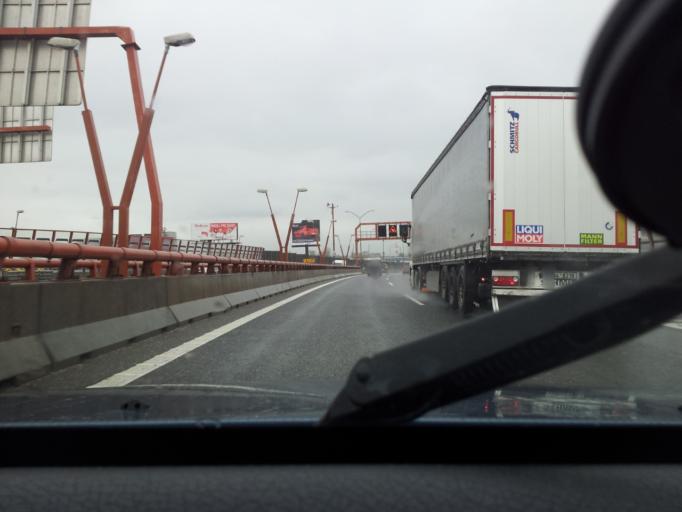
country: SK
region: Bratislavsky
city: Bratislava
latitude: 48.1480
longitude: 17.1804
